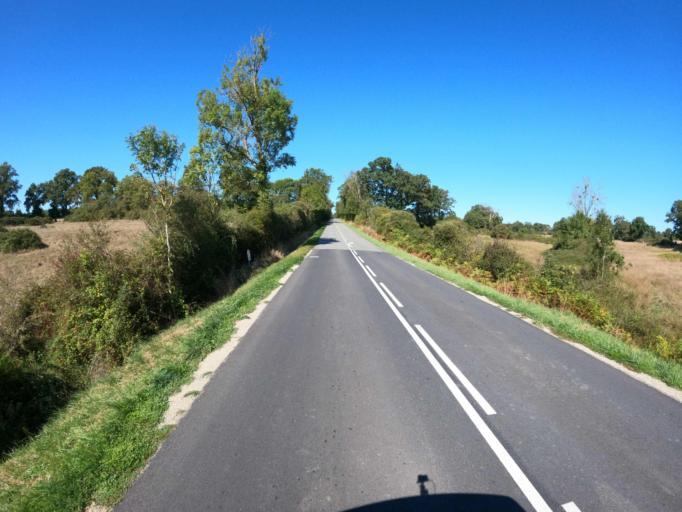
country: FR
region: Limousin
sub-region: Departement de la Haute-Vienne
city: Le Dorat
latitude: 46.2595
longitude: 1.0376
